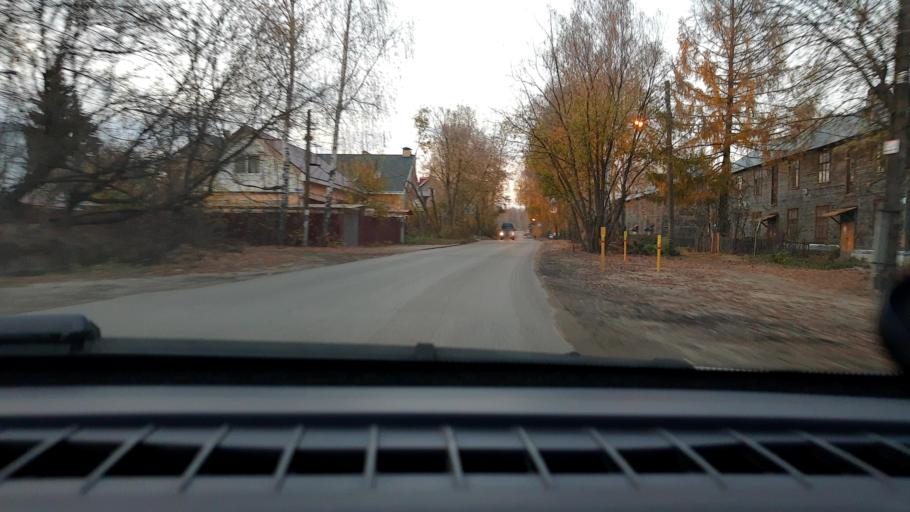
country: RU
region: Nizjnij Novgorod
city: Gorbatovka
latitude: 56.3440
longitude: 43.8308
